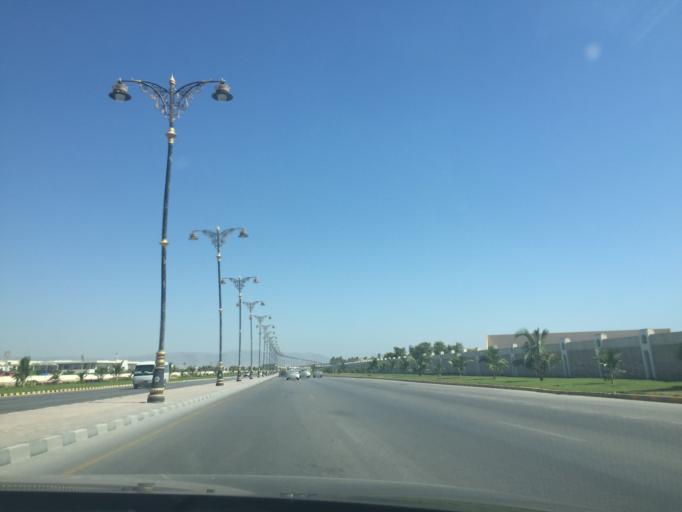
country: OM
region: Zufar
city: Salalah
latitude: 17.0251
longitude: 54.1243
